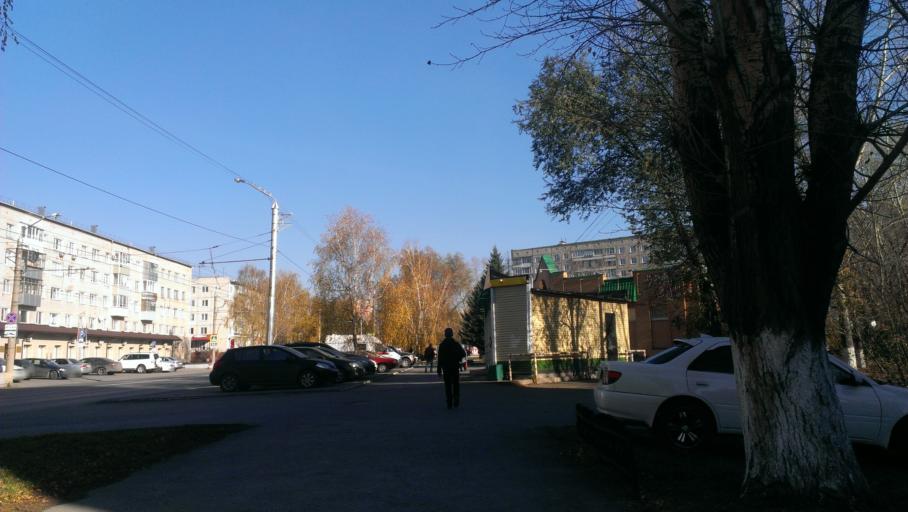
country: RU
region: Altai Krai
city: Novosilikatnyy
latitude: 53.3477
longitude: 83.6856
